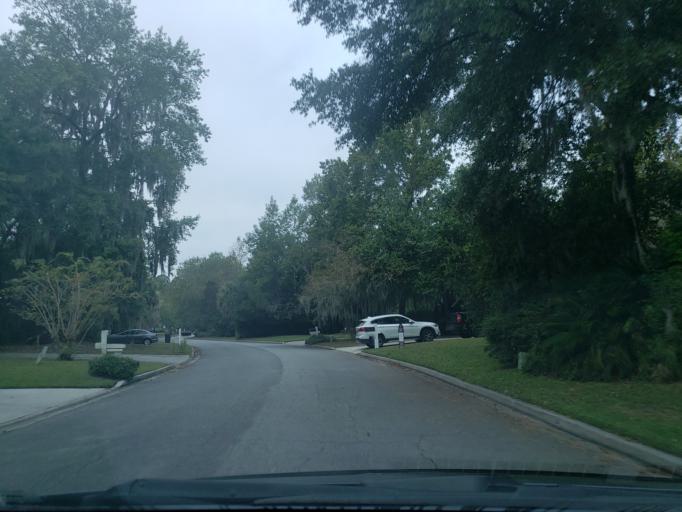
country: US
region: Georgia
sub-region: Chatham County
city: Isle of Hope
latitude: 31.9740
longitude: -81.0814
